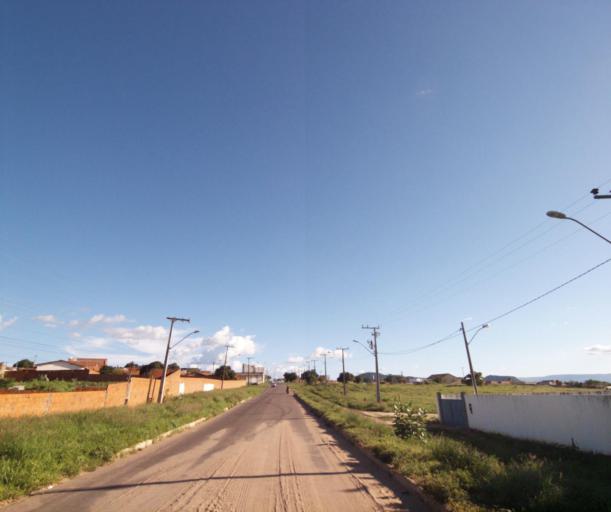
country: BR
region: Bahia
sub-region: Guanambi
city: Guanambi
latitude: -14.2128
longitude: -42.8039
